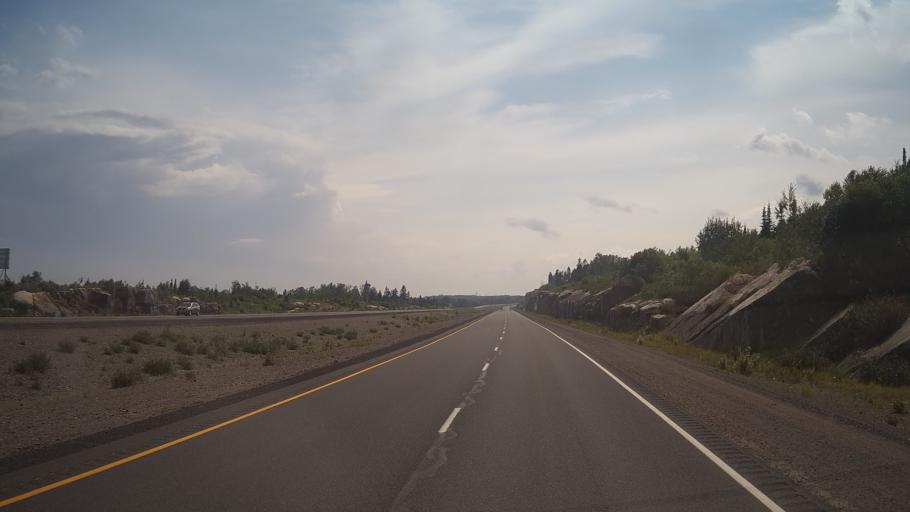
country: CA
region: Ontario
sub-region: Thunder Bay District
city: Thunder Bay
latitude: 48.5525
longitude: -88.9034
